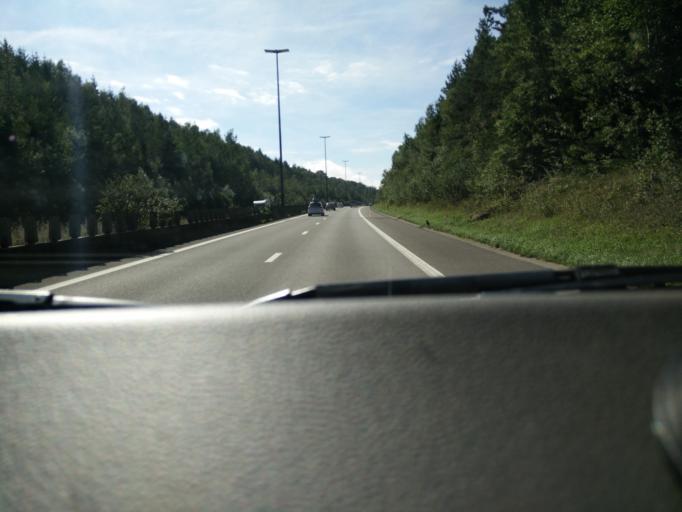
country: BE
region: Wallonia
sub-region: Province du Luxembourg
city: Tellin
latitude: 50.0490
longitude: 5.2112
